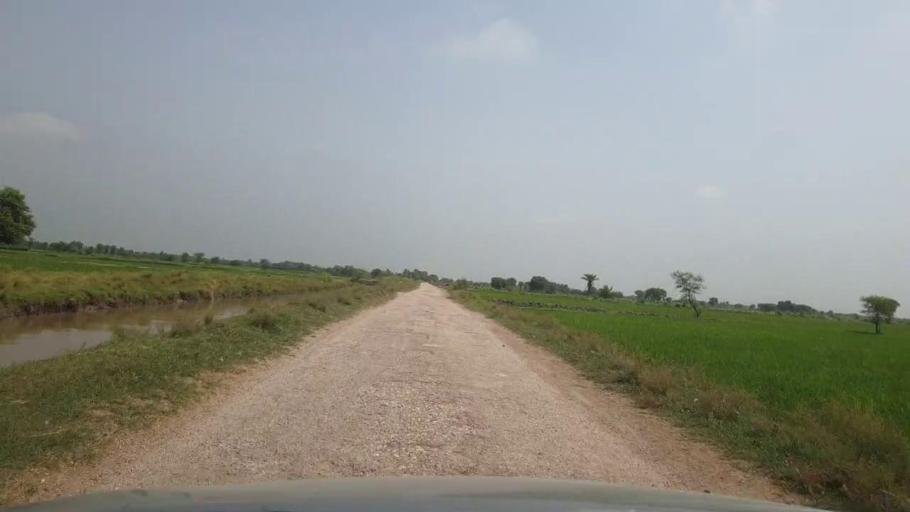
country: PK
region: Sindh
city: Ratodero
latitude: 27.9281
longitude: 68.3606
